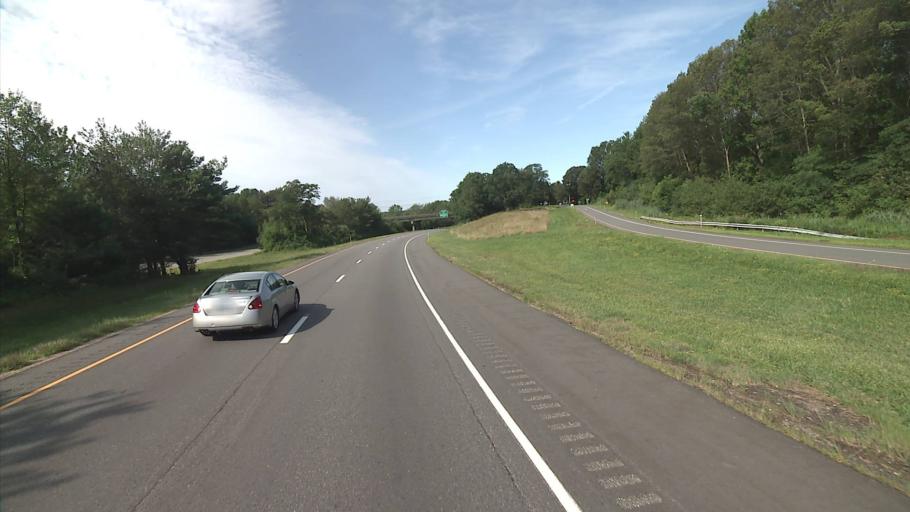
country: US
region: Connecticut
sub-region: New London County
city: Colchester
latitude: 41.5639
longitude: -72.3142
